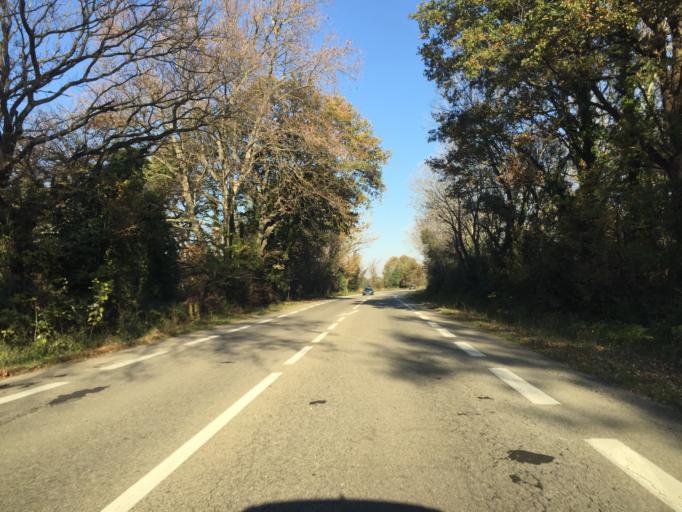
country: FR
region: Provence-Alpes-Cote d'Azur
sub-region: Departement du Vaucluse
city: Jonquieres
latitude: 44.1101
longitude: 4.9190
